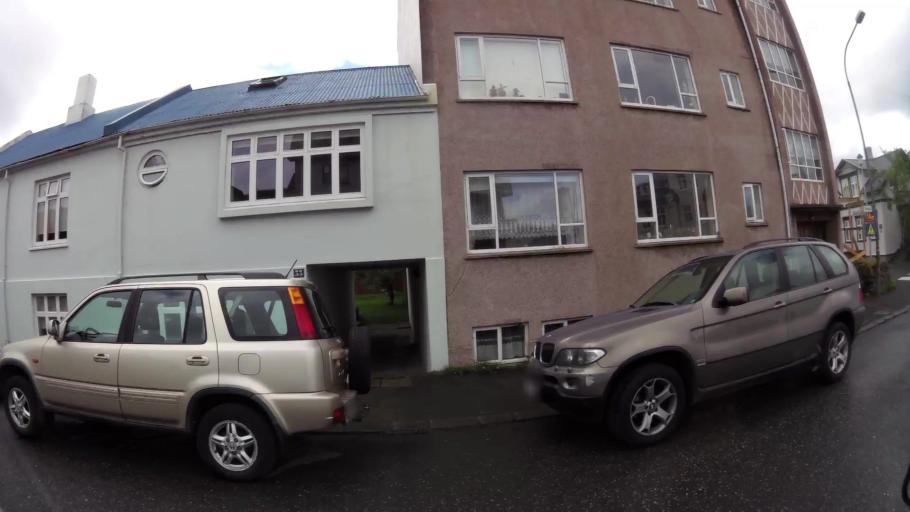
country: IS
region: Capital Region
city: Seltjarnarnes
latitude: 64.1496
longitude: -21.9520
